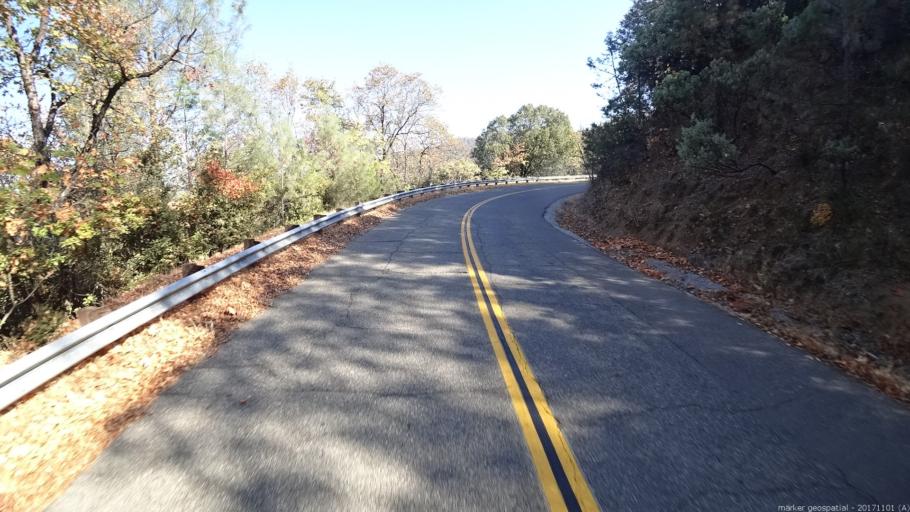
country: US
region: California
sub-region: Shasta County
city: Central Valley (historical)
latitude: 40.7142
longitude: -122.4128
